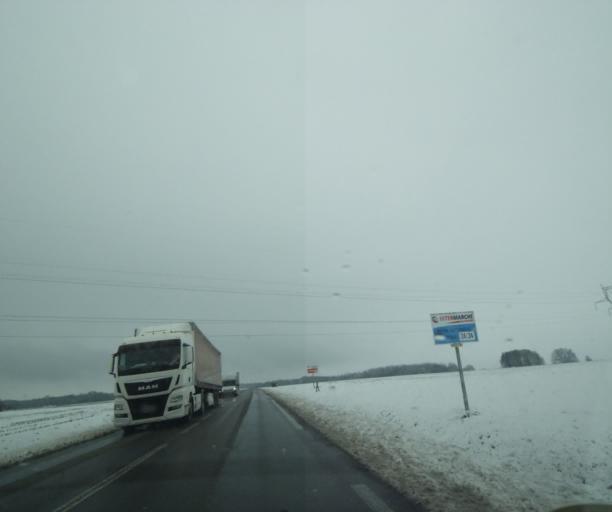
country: FR
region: Champagne-Ardenne
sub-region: Departement de la Haute-Marne
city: Montier-en-Der
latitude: 48.5038
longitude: 4.7892
